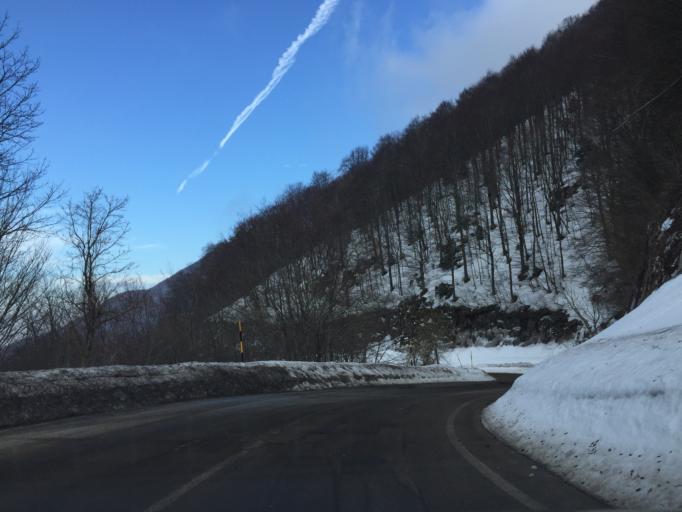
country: IT
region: Molise
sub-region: Provincia di Campobasso
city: San Massimo
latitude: 41.4668
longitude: 14.4064
